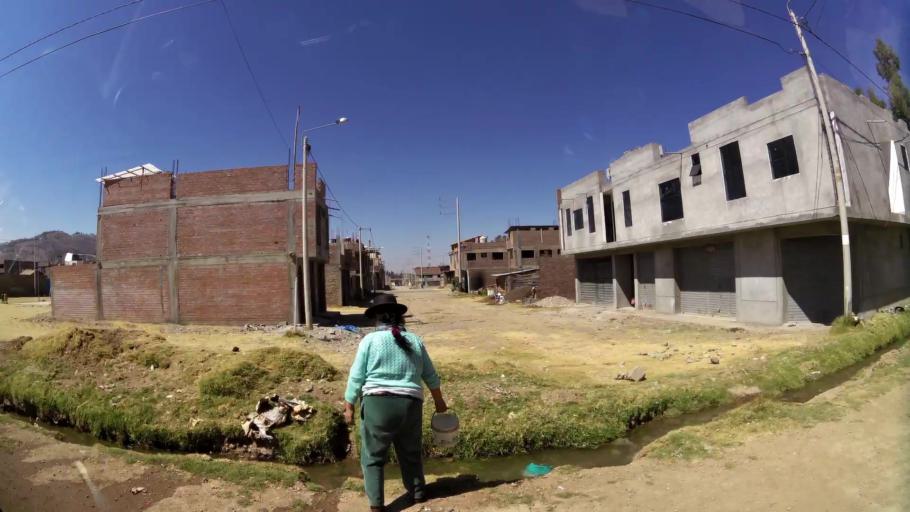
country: PE
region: Junin
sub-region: Provincia de Concepcion
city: Concepcion
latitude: -11.9161
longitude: -75.3210
